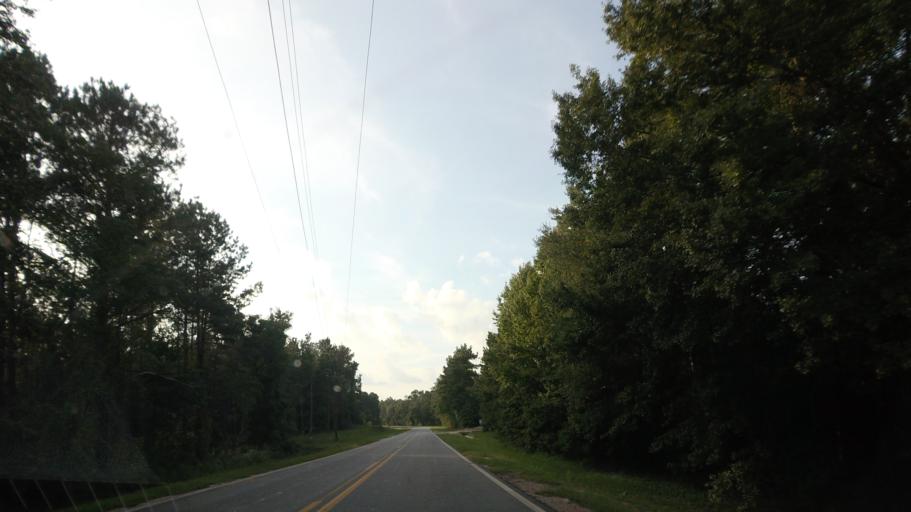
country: US
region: Georgia
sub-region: Wilkinson County
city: Gordon
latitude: 32.8212
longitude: -83.4043
